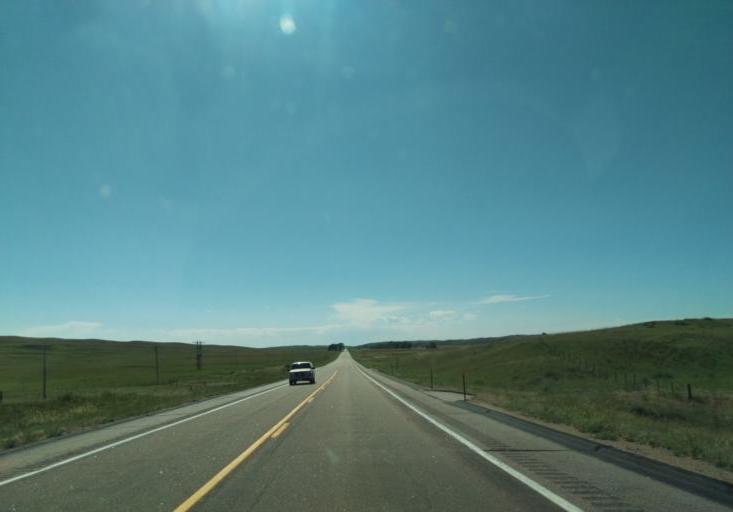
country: US
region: South Dakota
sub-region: Bennett County
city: Martin
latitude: 42.9214
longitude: -101.5423
